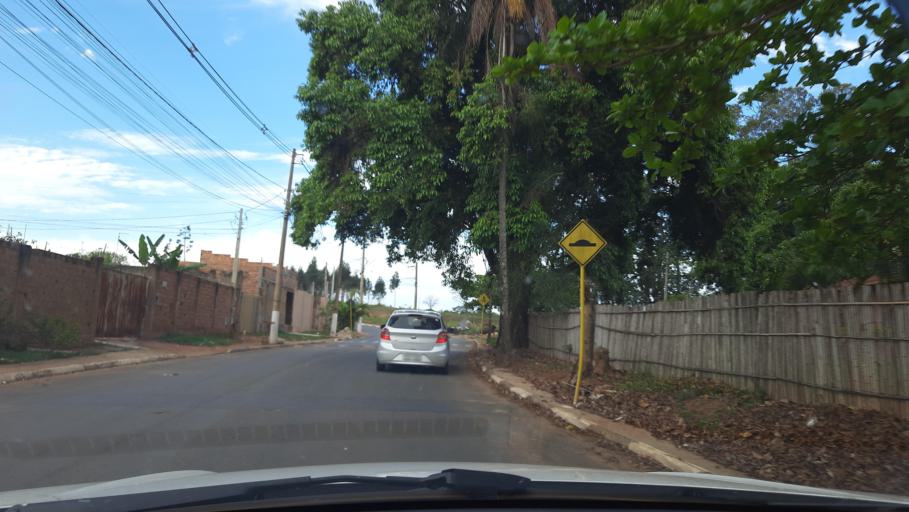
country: BR
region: Sao Paulo
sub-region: Casa Branca
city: Casa Branca
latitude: -21.7647
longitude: -47.0862
